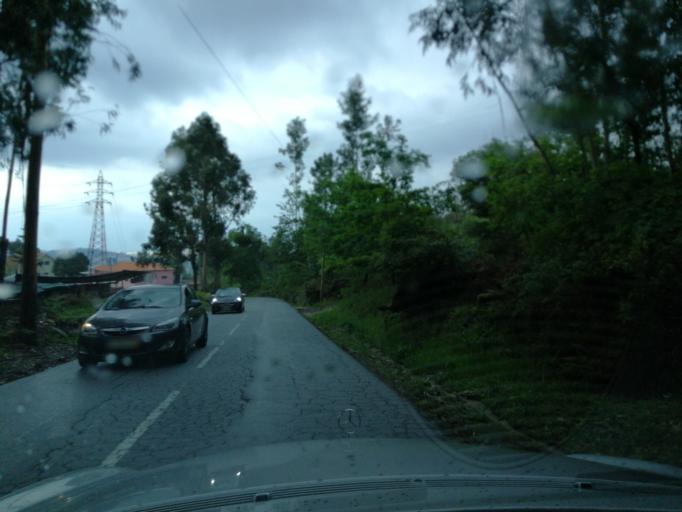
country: PT
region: Braga
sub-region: Vila Nova de Famalicao
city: Joane
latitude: 41.4728
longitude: -8.4282
